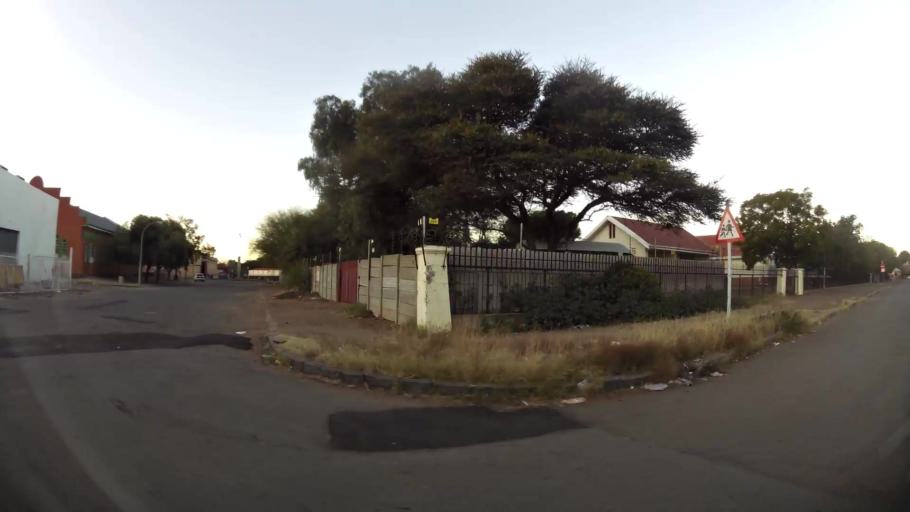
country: ZA
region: Northern Cape
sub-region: Frances Baard District Municipality
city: Kimberley
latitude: -28.7320
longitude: 24.7649
